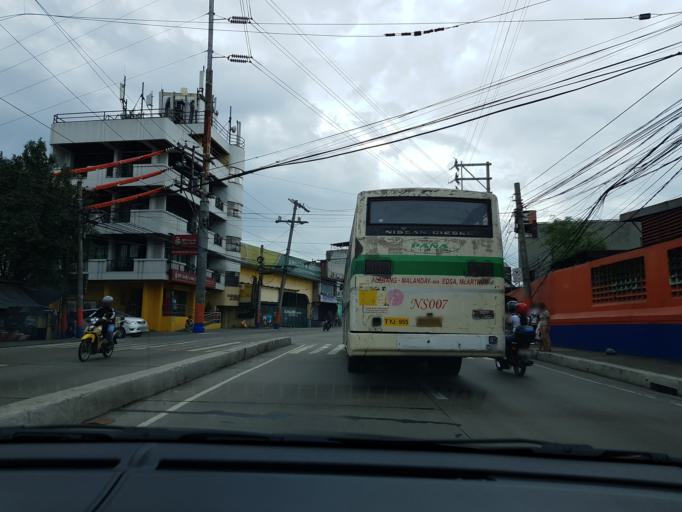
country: PH
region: Metro Manila
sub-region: Caloocan City
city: Niugan
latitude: 14.6658
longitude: 120.9840
